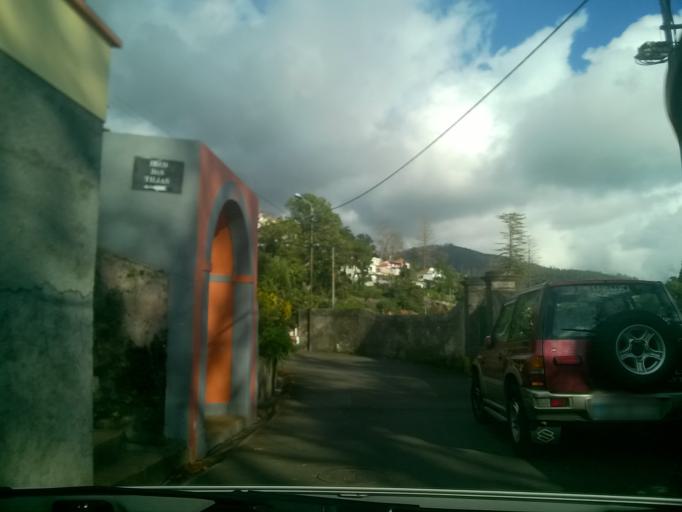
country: PT
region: Madeira
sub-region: Funchal
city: Nossa Senhora do Monte
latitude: 32.6775
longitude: -16.9039
